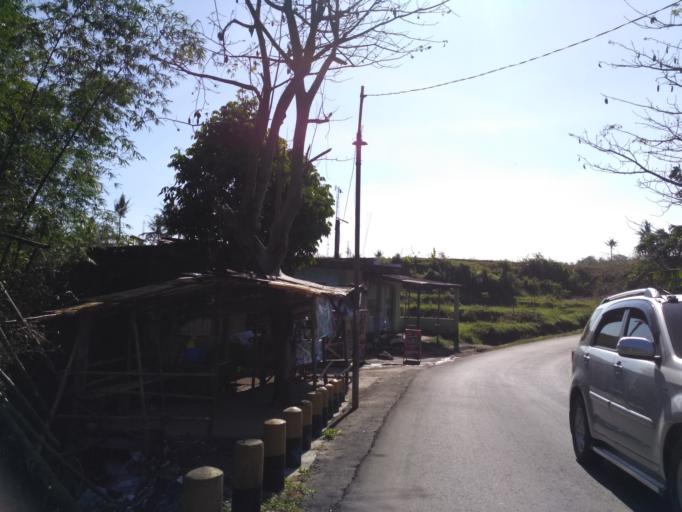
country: ID
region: East Java
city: Singosari
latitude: -7.9301
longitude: 112.6628
